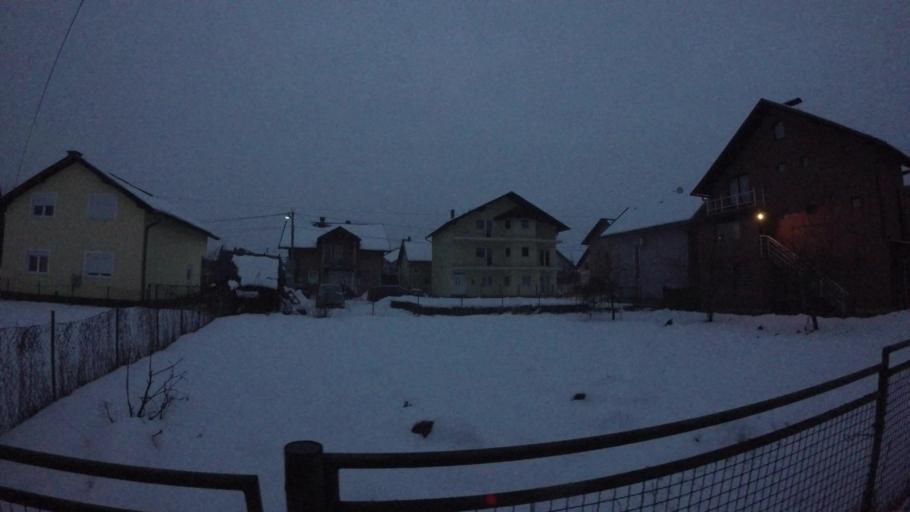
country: BA
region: Federation of Bosnia and Herzegovina
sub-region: Kanton Sarajevo
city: Sarajevo
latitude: 43.8558
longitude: 18.2911
